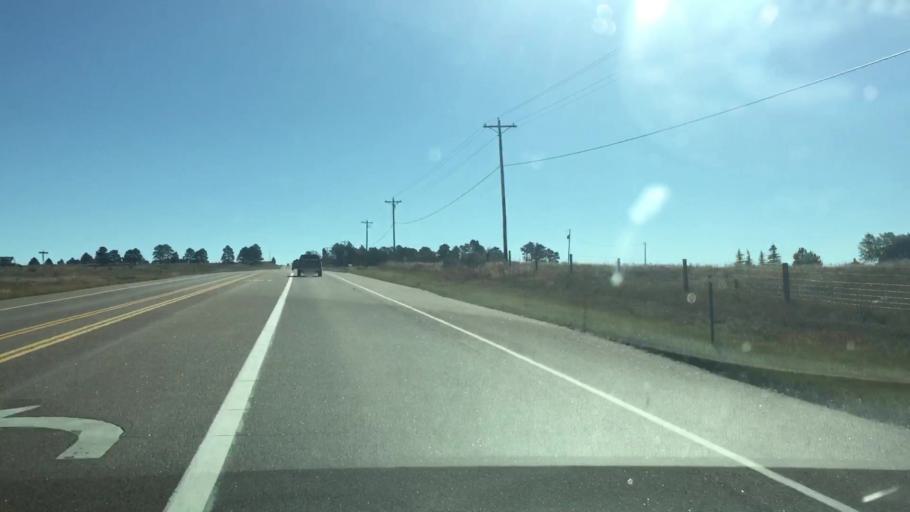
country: US
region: Colorado
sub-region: Elbert County
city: Elizabeth
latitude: 39.3584
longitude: -104.5322
